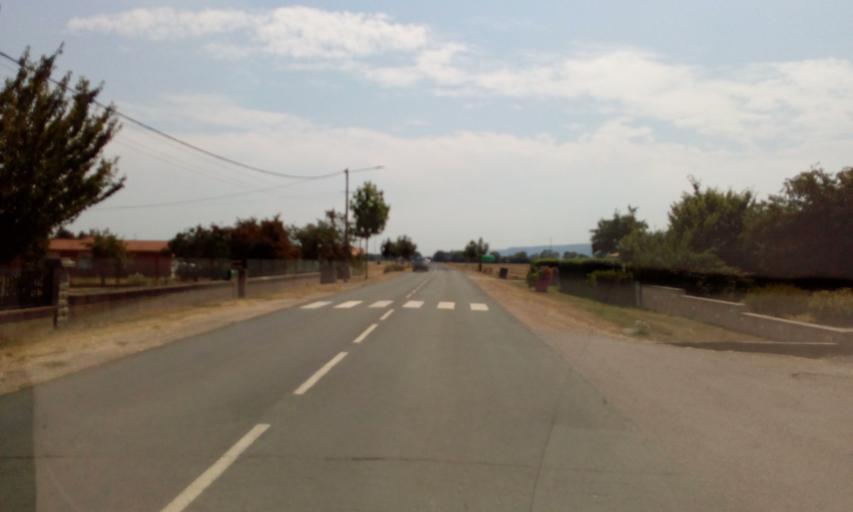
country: FR
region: Lorraine
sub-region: Departement de la Meuse
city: Etain
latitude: 49.0920
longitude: 5.6271
